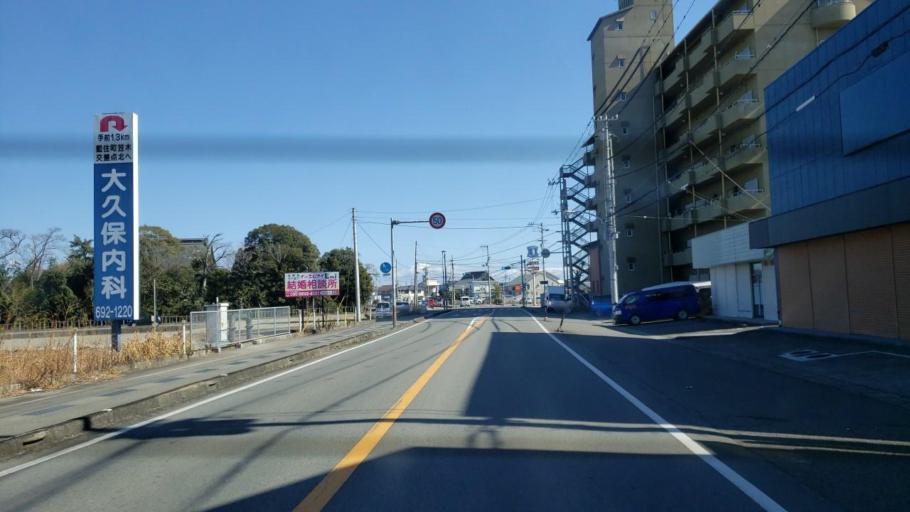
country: JP
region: Tokushima
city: Tokushima-shi
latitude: 34.1317
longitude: 134.5214
